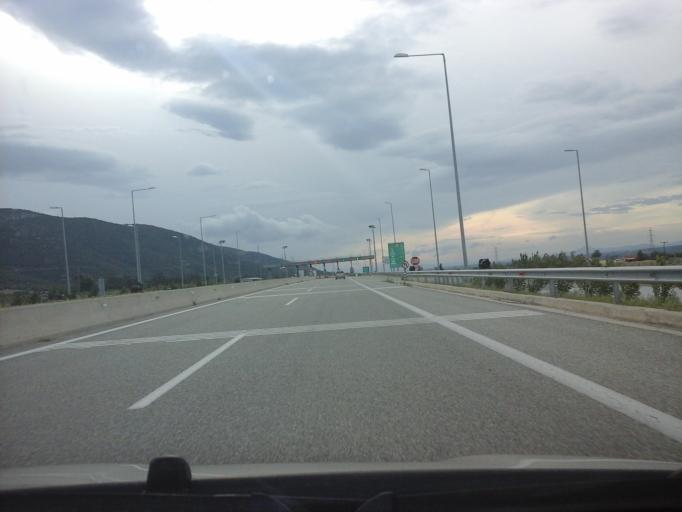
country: GR
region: East Macedonia and Thrace
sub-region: Nomos Xanthis
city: Selero
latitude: 41.1204
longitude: 25.0772
